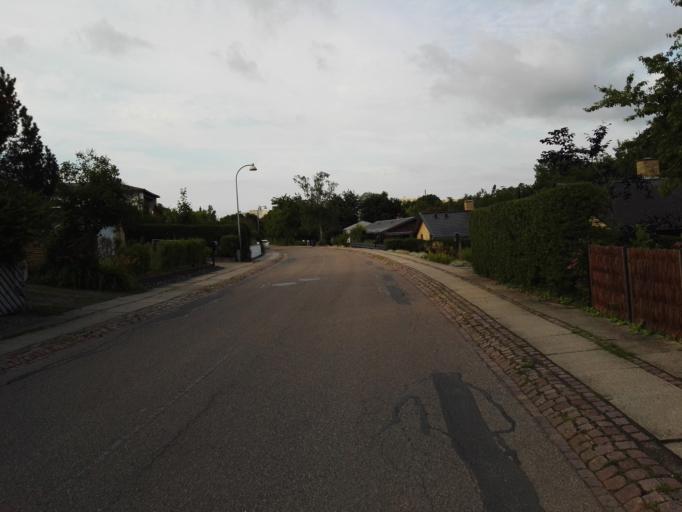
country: DK
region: Capital Region
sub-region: Ballerup Kommune
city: Malov
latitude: 55.7559
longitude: 12.3179
